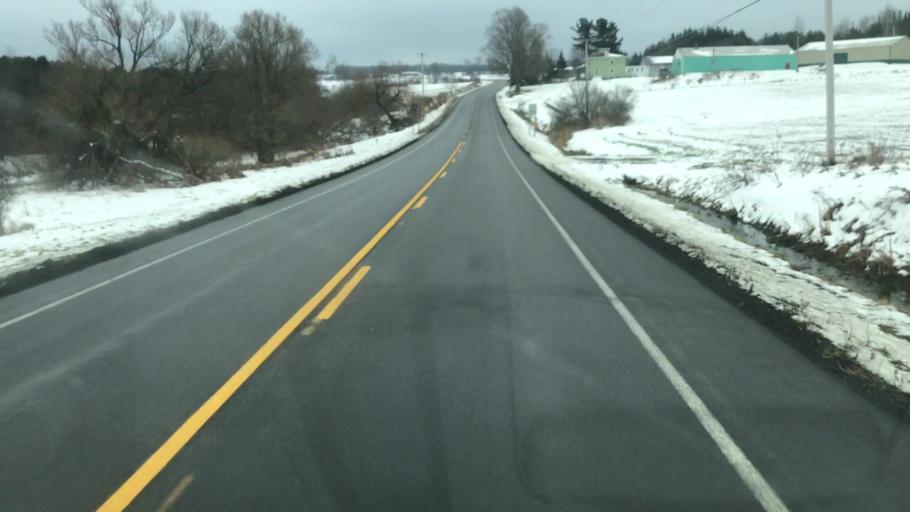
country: US
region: New York
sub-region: Cayuga County
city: Moravia
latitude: 42.7938
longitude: -76.3471
